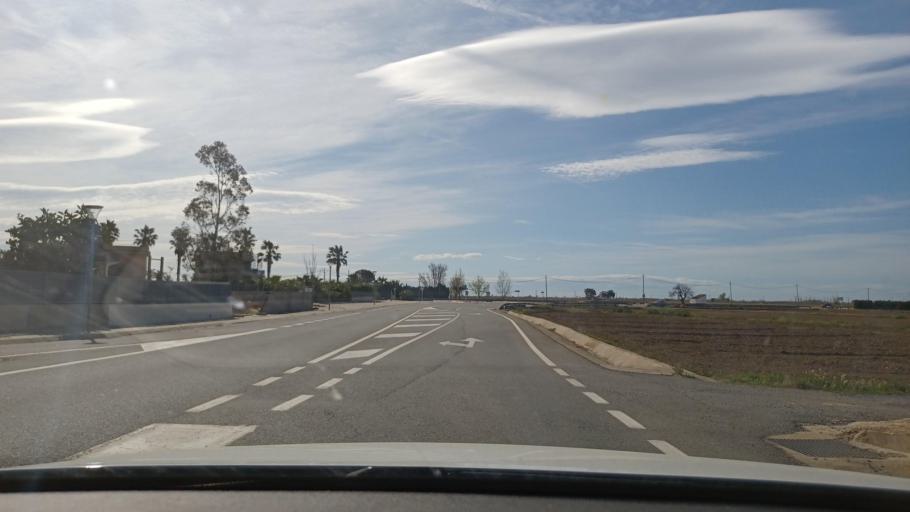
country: ES
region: Catalonia
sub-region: Provincia de Tarragona
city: L'Ampolla
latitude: 40.7995
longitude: 0.6956
